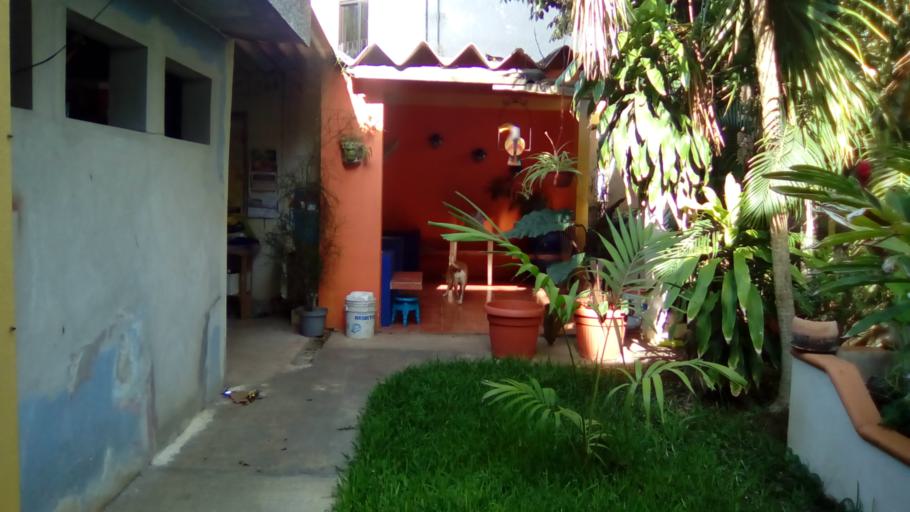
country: MX
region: Campeche
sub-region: Campeche
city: Campeche
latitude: 19.8360
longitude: -90.5252
